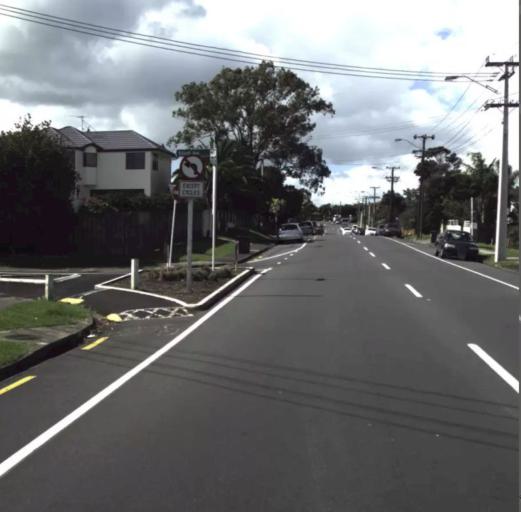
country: NZ
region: Auckland
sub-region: Auckland
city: North Shore
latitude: -36.7745
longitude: 174.7177
